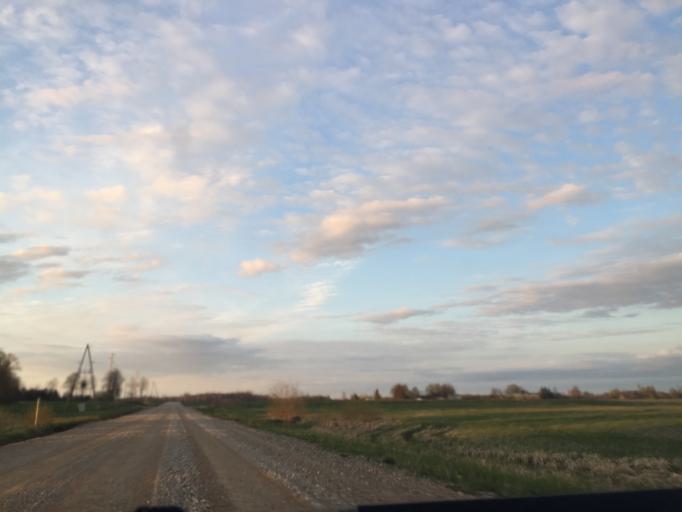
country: LV
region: Gulbenes Rajons
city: Gulbene
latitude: 57.1959
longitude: 26.7620
